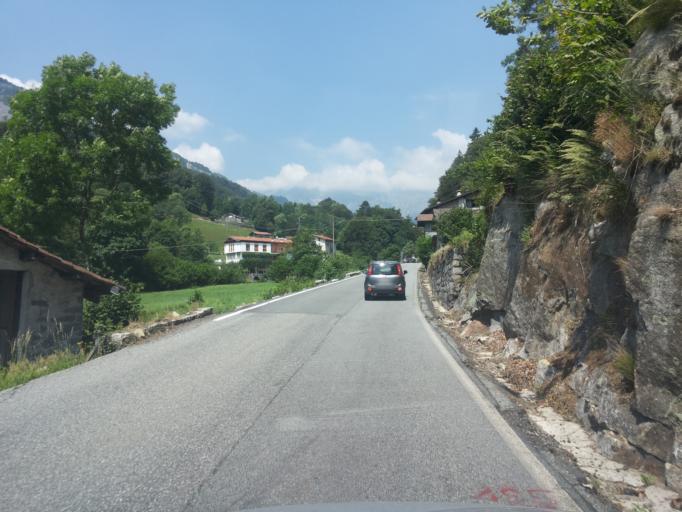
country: IT
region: Piedmont
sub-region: Provincia di Biella
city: Quittengo
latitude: 45.6556
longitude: 8.0091
